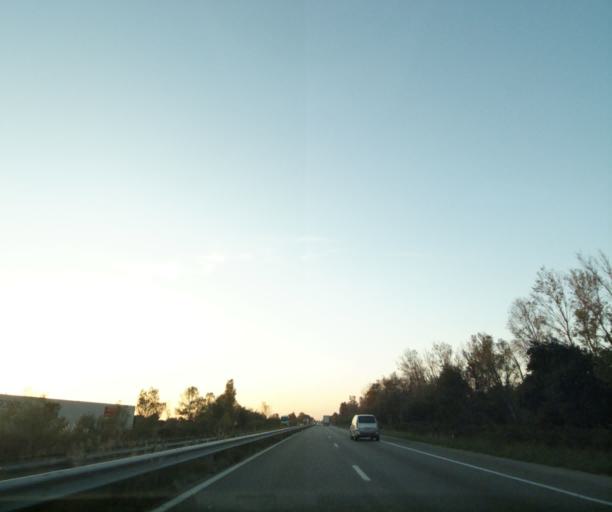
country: FR
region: Provence-Alpes-Cote d'Azur
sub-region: Departement des Bouches-du-Rhone
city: Saint-Martin-de-Crau
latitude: 43.6306
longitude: 4.7968
